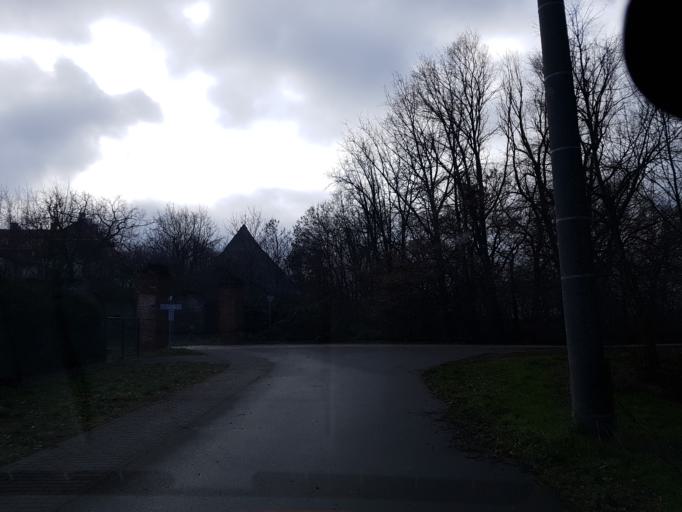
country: DE
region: Brandenburg
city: Muhlberg
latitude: 51.4743
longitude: 13.2034
